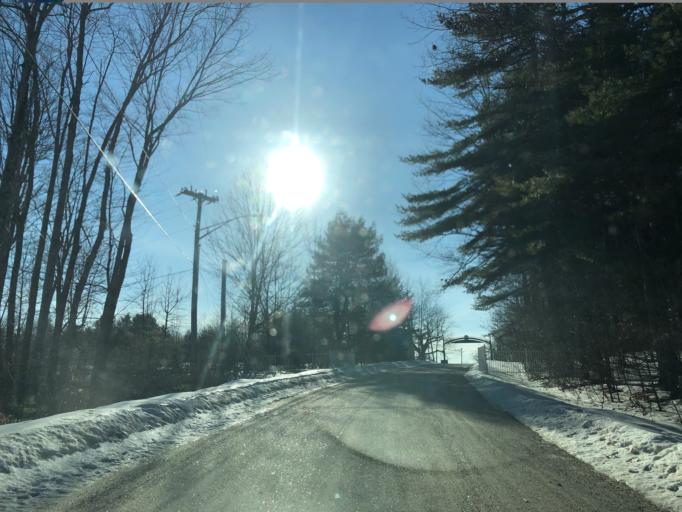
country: US
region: Maine
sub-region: Androscoggin County
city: Poland
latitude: 44.0278
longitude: -70.3592
